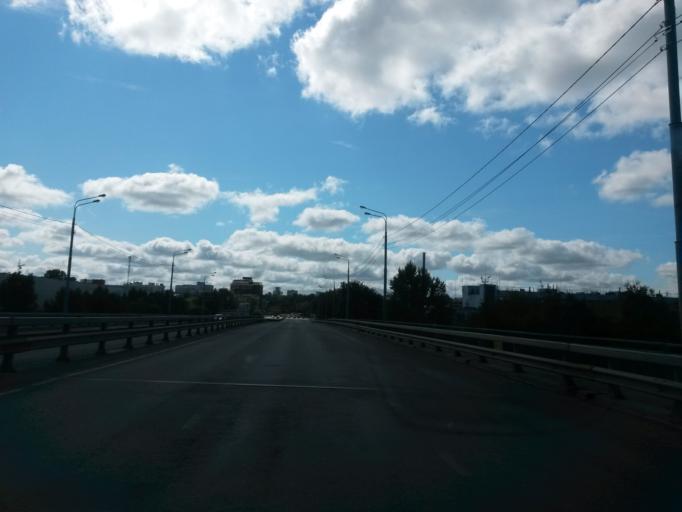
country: RU
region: Jaroslavl
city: Yaroslavl
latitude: 57.6124
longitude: 39.8595
